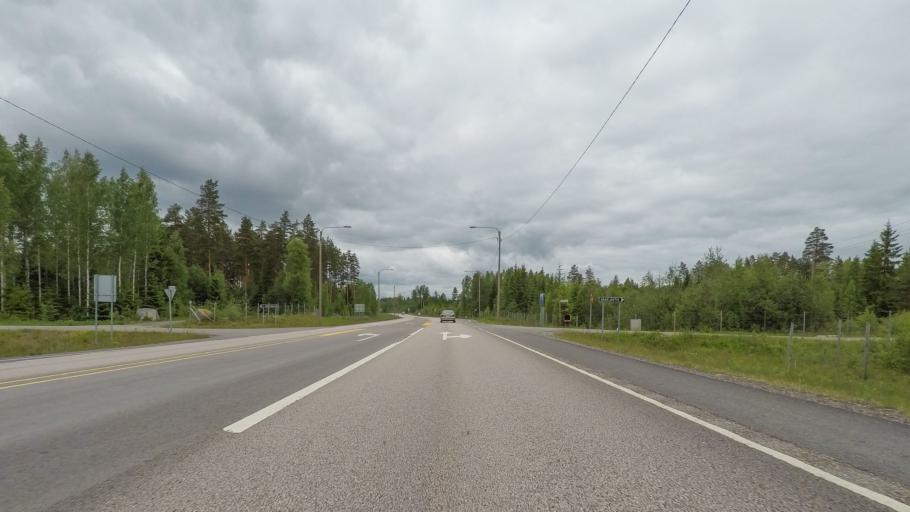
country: FI
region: Central Finland
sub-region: Joutsa
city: Joutsa
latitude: 61.8231
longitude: 26.0977
